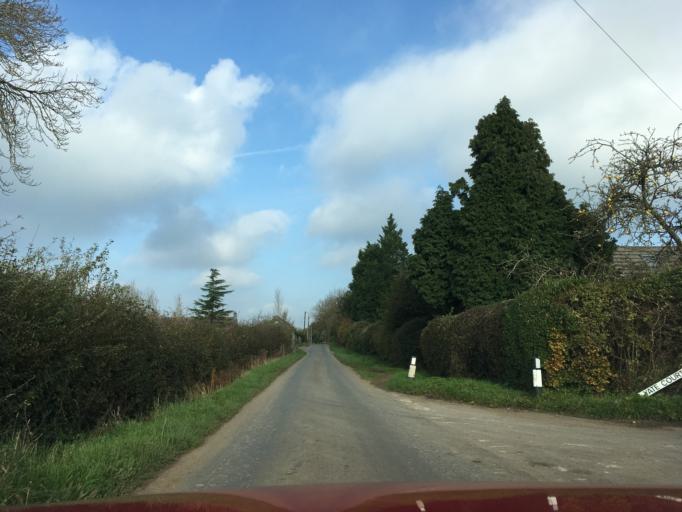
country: GB
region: England
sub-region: South Gloucestershire
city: Yate
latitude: 51.5695
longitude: -2.4252
